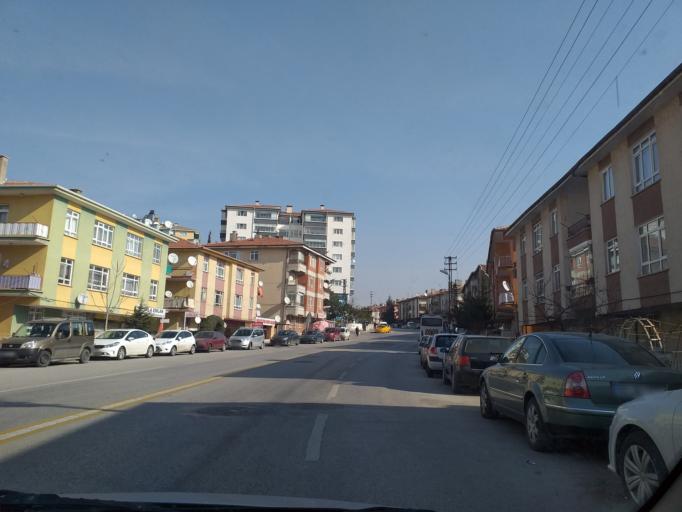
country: TR
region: Ankara
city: Ankara
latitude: 39.9881
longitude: 32.8546
